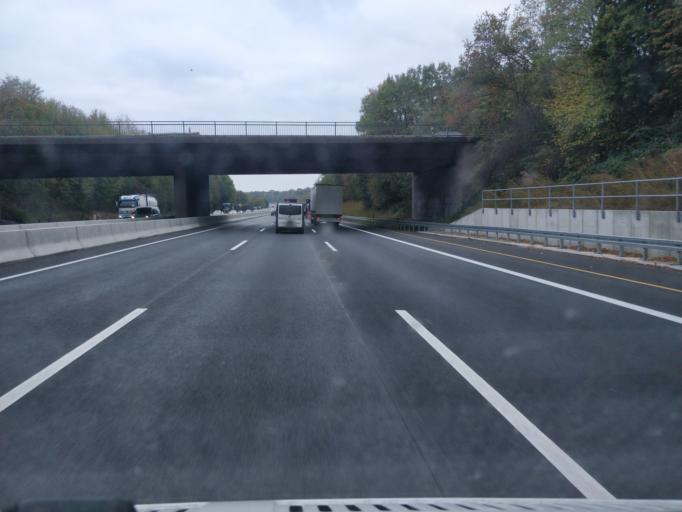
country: DE
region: North Rhine-Westphalia
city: Opladen
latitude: 51.0732
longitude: 6.9879
